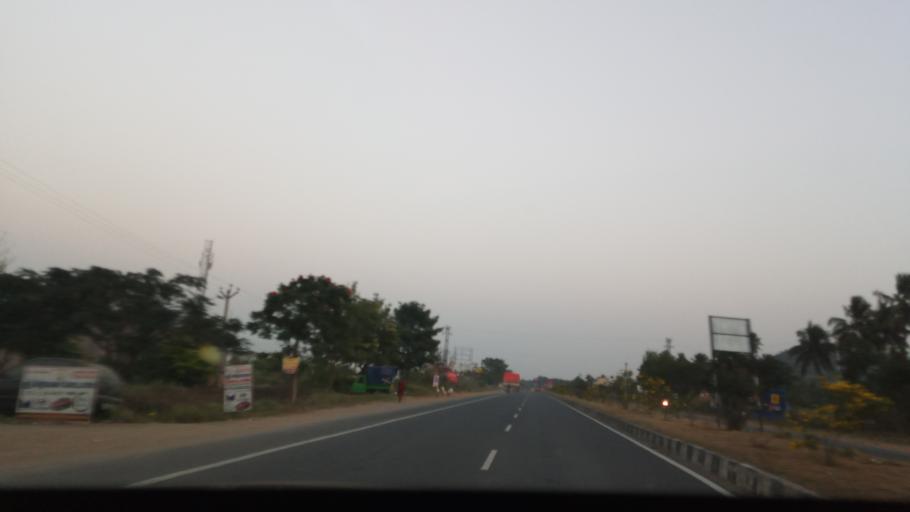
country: IN
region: Tamil Nadu
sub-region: Salem
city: Belur
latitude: 11.6598
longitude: 78.3333
